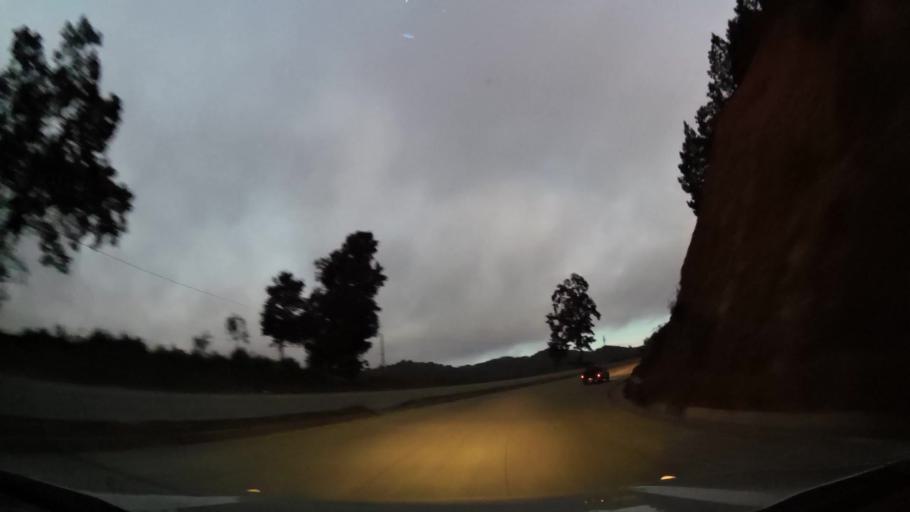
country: GT
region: Chimaltenango
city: Santa Apolonia
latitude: 14.8096
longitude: -90.9941
